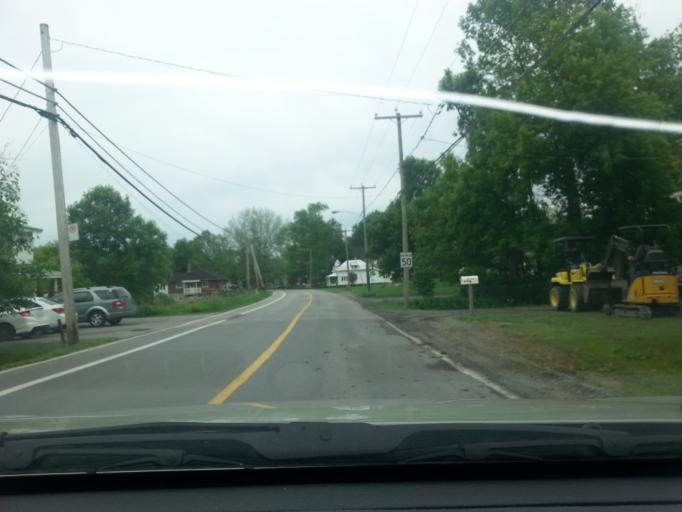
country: CA
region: Quebec
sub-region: Lanaudiere
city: Mascouche
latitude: 45.7017
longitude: -73.5621
